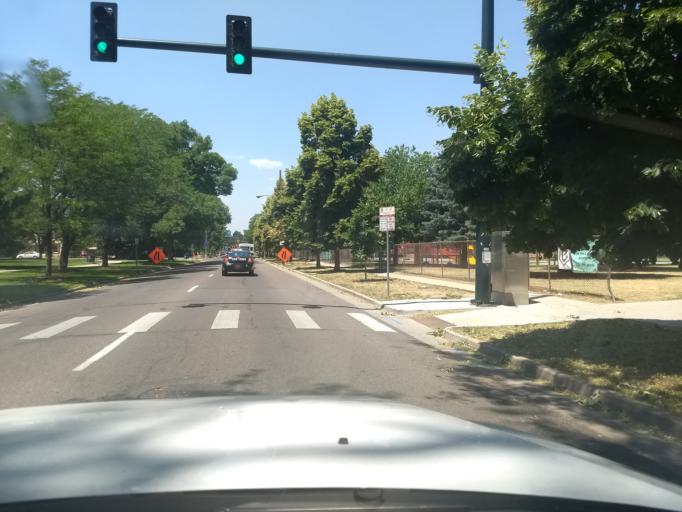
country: US
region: Colorado
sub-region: Denver County
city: Denver
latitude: 39.7620
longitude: -104.9696
